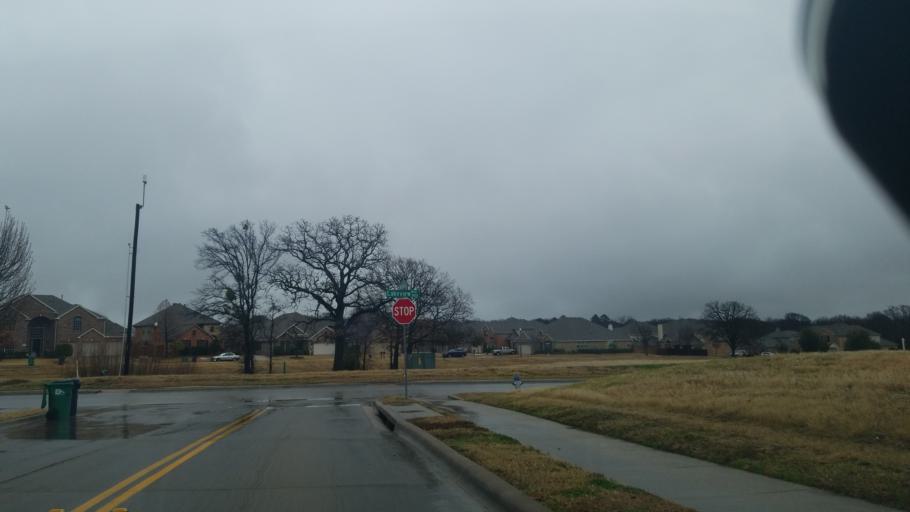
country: US
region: Texas
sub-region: Denton County
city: Corinth
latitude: 33.1780
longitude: -97.0587
